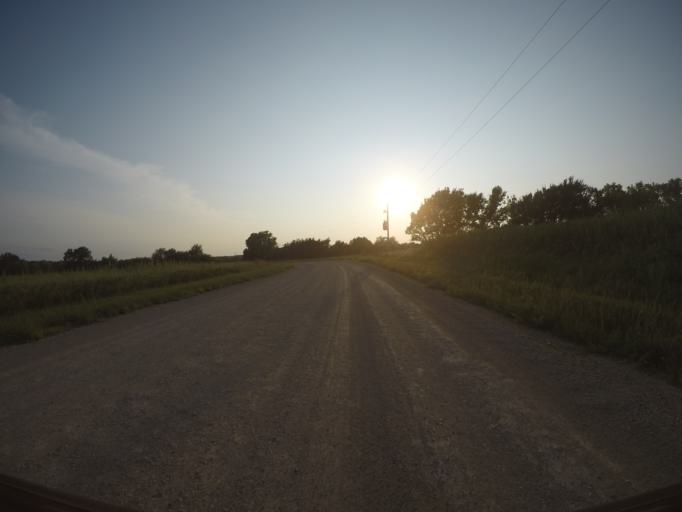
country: US
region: Kansas
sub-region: Riley County
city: Manhattan
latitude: 39.1304
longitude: -96.4679
